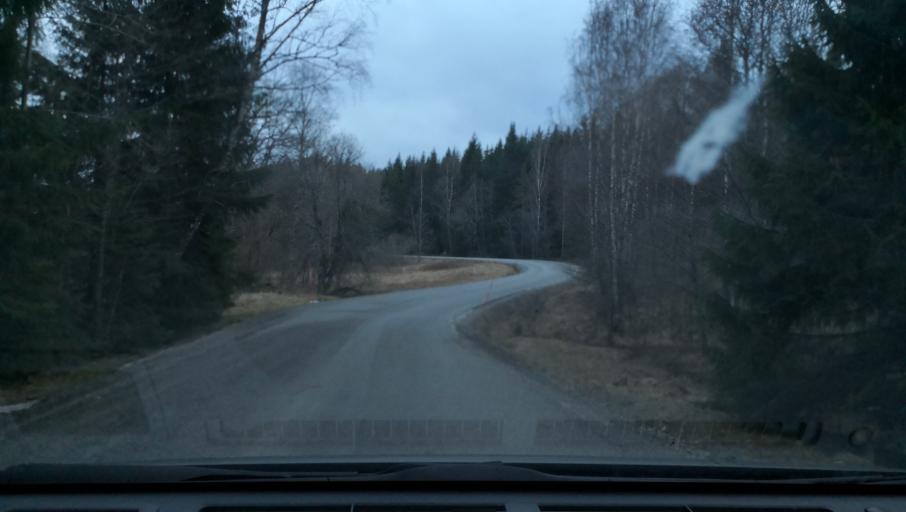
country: SE
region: Vaestmanland
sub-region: Kopings Kommun
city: Kolsva
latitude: 59.5686
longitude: 15.7751
